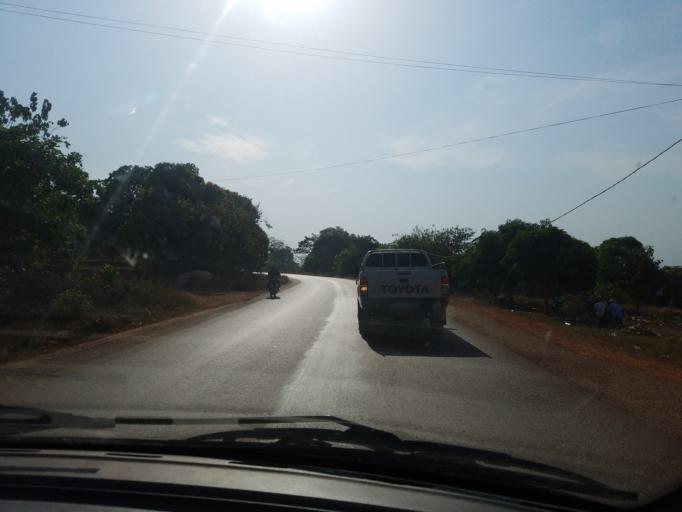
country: GN
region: Boke
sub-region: Boke Prefecture
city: Boke
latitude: 10.9093
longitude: -14.3114
